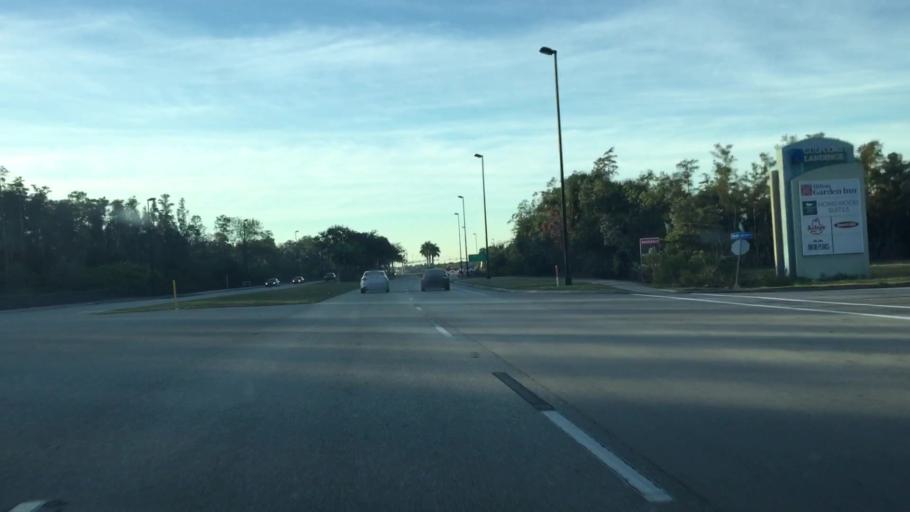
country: US
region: Florida
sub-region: Lee County
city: Three Oaks
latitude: 26.4975
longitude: -81.7838
